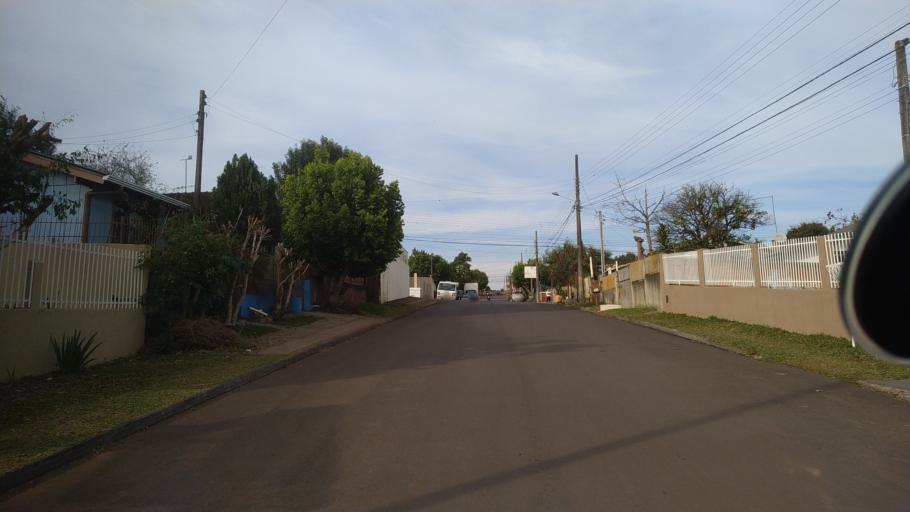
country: BR
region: Santa Catarina
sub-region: Chapeco
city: Chapeco
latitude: -27.1186
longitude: -52.6242
